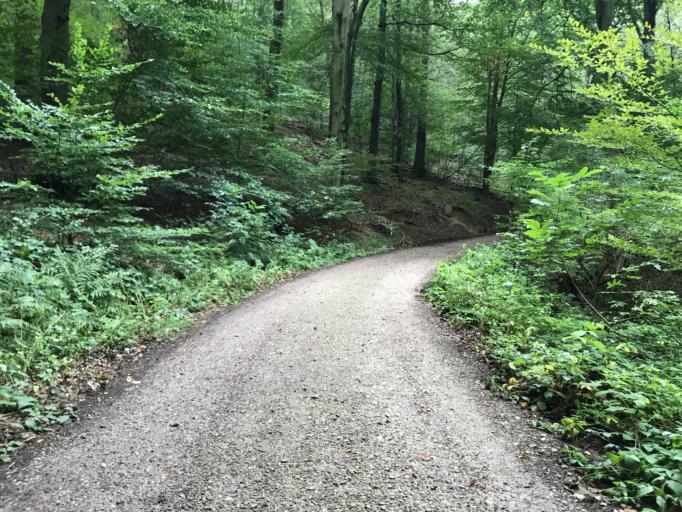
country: DE
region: Baden-Wuerttemberg
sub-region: Karlsruhe Region
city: Heidelberg
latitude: 49.4225
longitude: 8.6998
